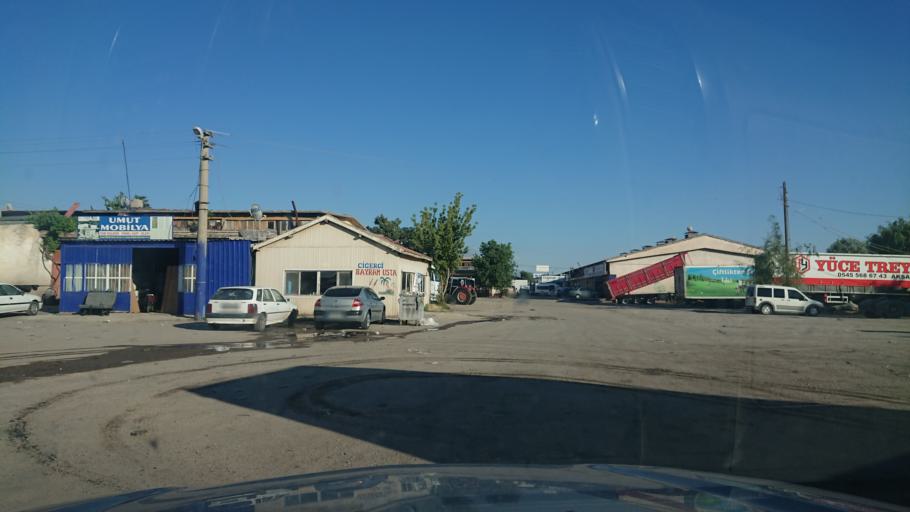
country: TR
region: Aksaray
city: Aksaray
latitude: 38.3742
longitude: 33.9929
